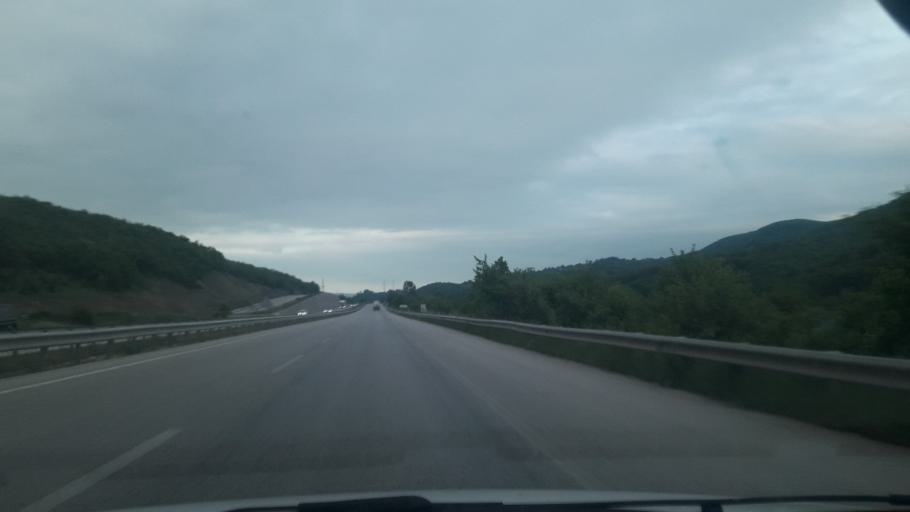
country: TR
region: Samsun
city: Kavak
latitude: 41.0517
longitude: 35.9412
